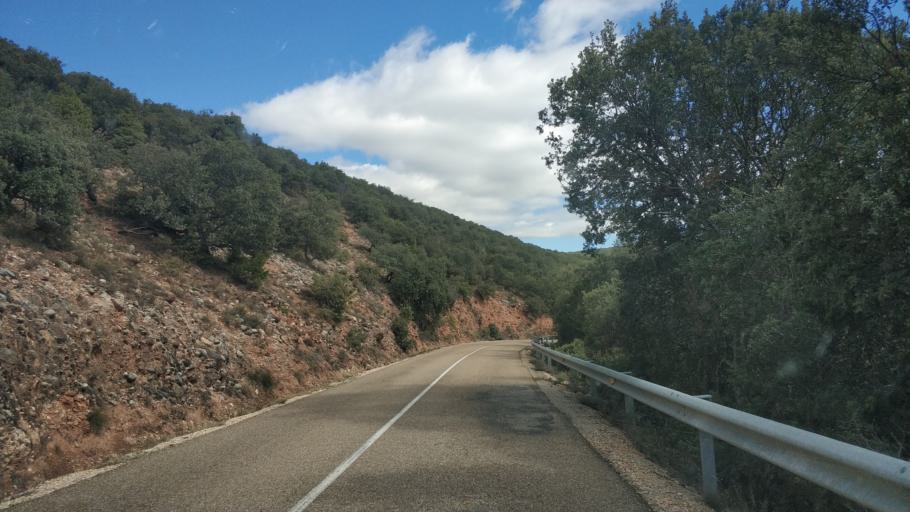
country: ES
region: Castille and Leon
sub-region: Provincia de Burgos
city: Retuerta
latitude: 42.0413
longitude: -3.4910
